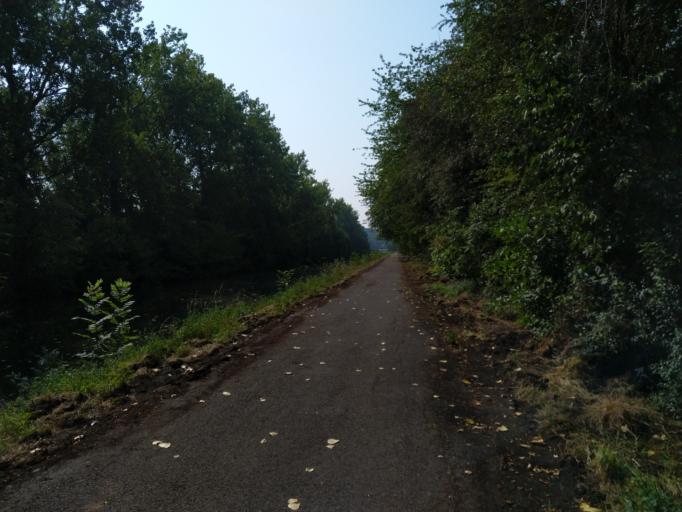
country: BE
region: Wallonia
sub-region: Province du Hainaut
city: Seneffe
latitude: 50.5198
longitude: 4.2648
